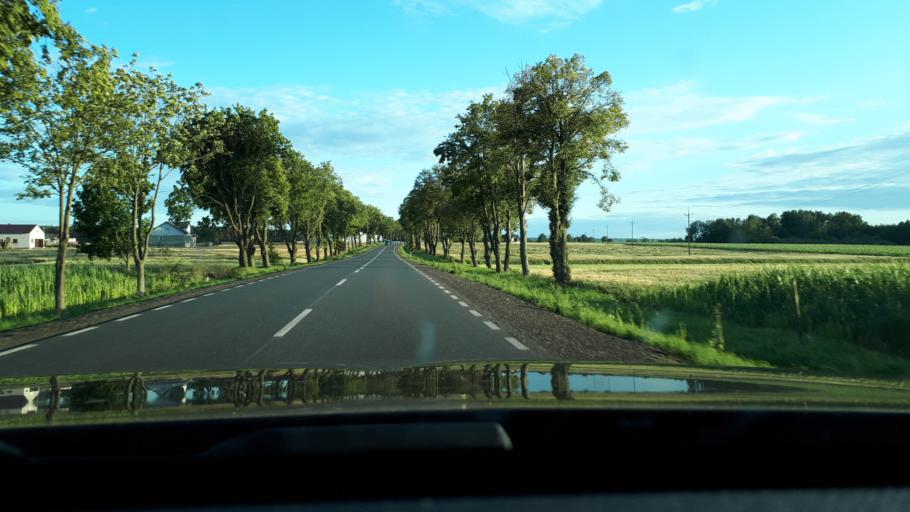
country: PL
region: Masovian Voivodeship
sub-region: Powiat ciechanowski
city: Ciechanow
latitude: 52.8233
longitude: 20.6153
